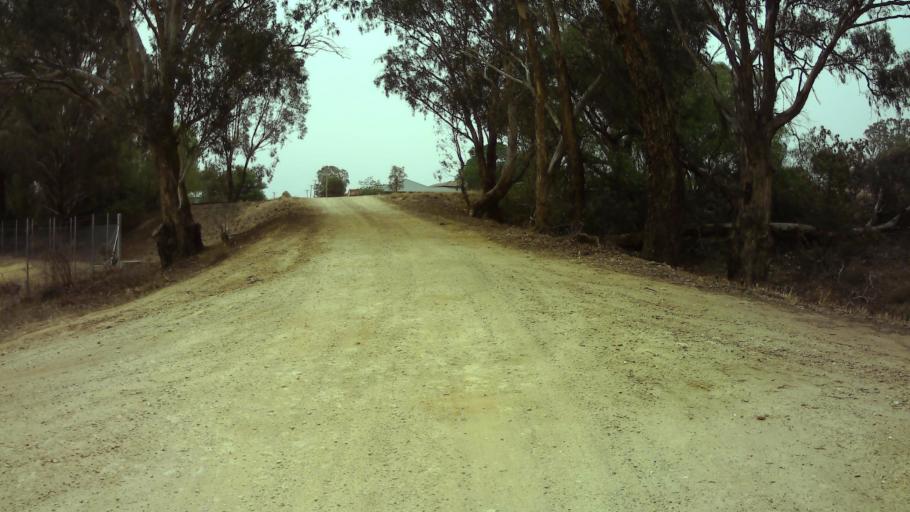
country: AU
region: New South Wales
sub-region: Weddin
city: Grenfell
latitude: -33.9036
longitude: 148.1545
